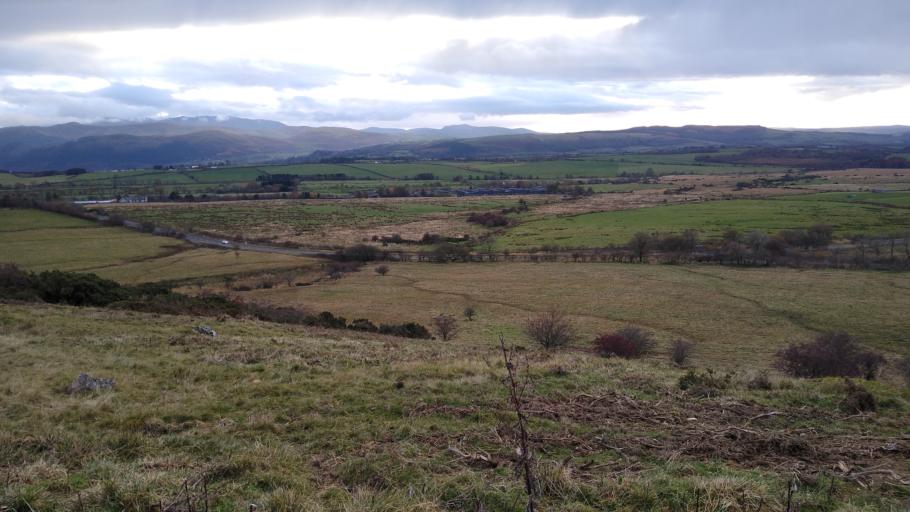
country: GB
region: England
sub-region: Cumbria
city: Aspatria
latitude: 54.7174
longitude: -3.2342
